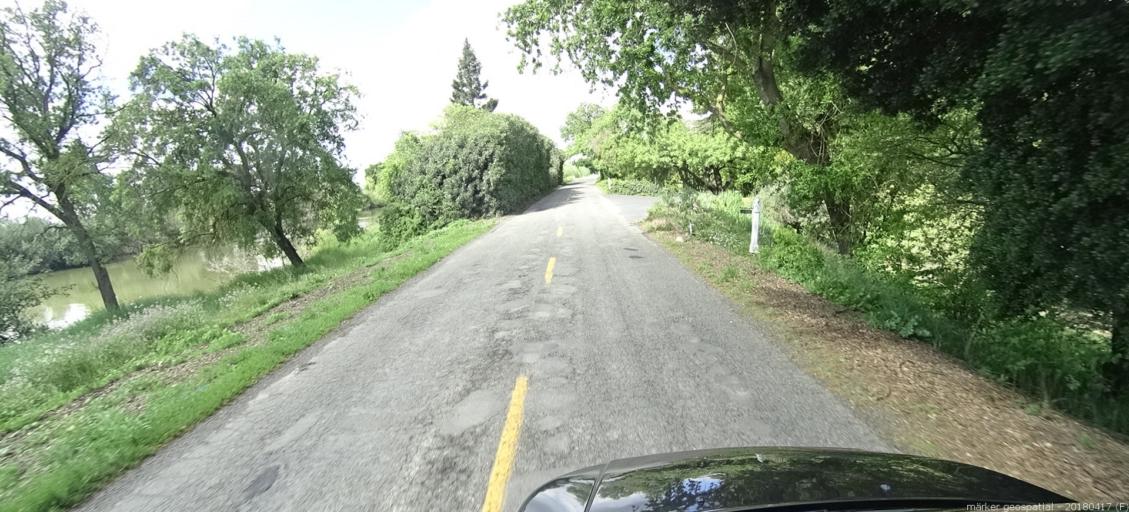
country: US
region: California
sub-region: Sacramento County
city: Walnut Grove
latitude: 38.2246
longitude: -121.5359
